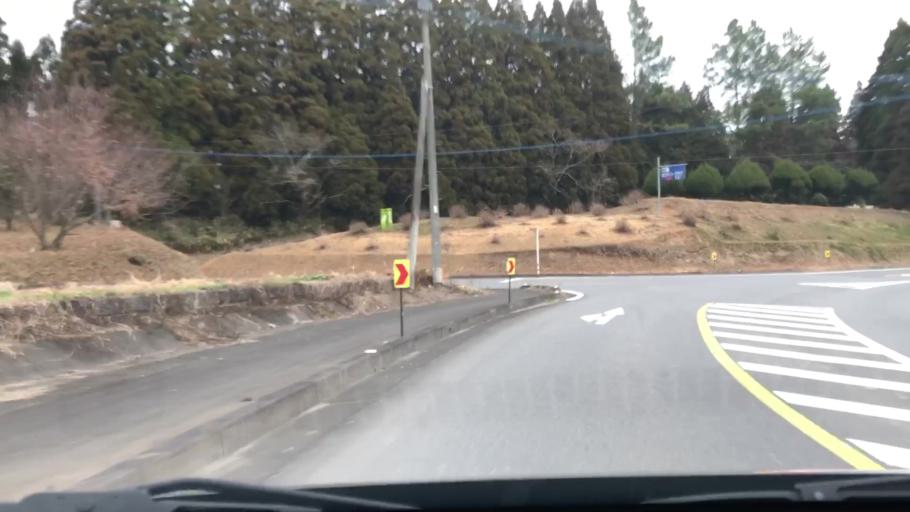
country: JP
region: Oita
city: Usuki
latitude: 33.0083
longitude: 131.6306
